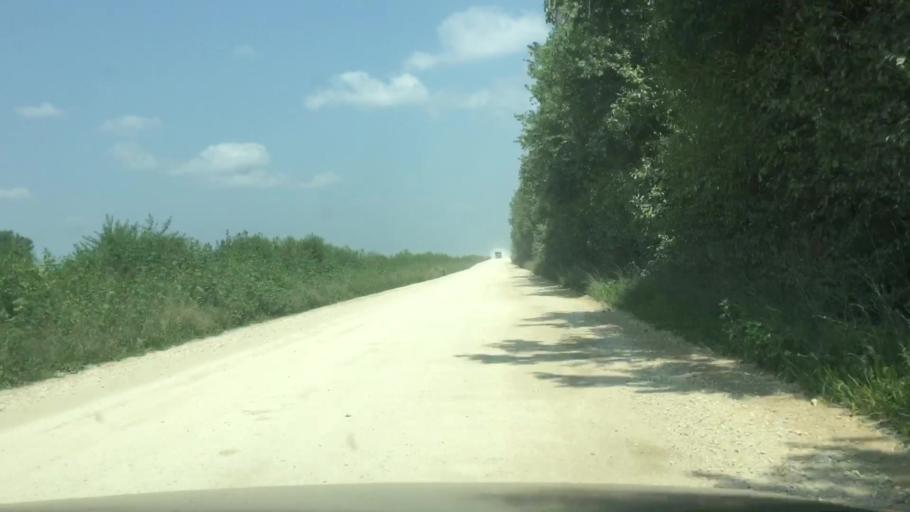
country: US
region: Kansas
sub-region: Allen County
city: Humboldt
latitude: 37.8296
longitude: -95.4093
